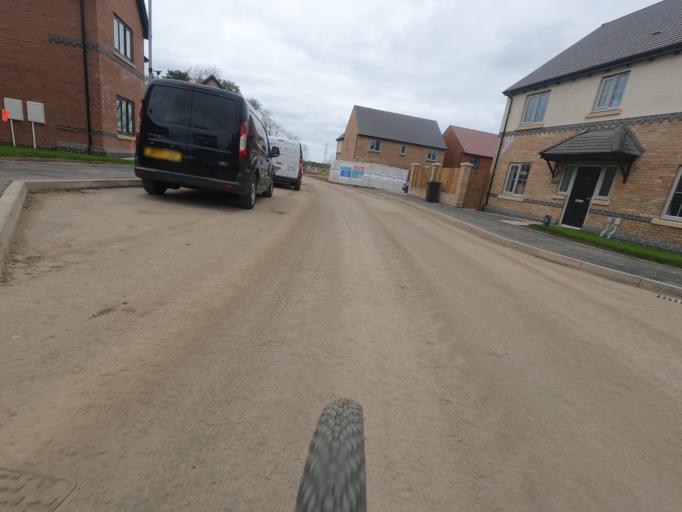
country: GB
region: England
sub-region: Northumberland
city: Ponteland
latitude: 55.0617
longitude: -1.7572
